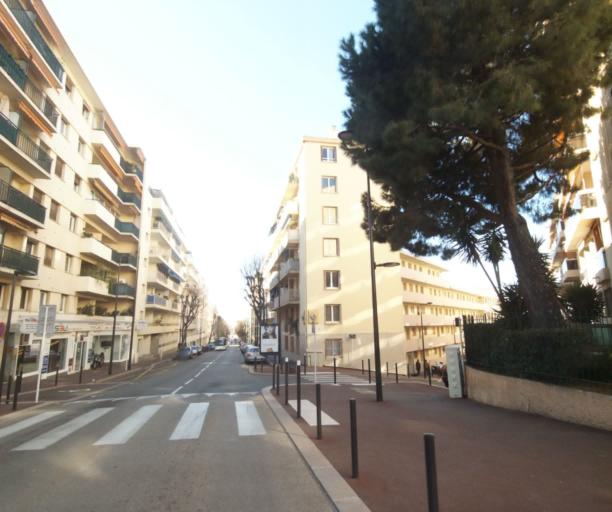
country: FR
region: Provence-Alpes-Cote d'Azur
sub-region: Departement des Alpes-Maritimes
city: Antibes
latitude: 43.5738
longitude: 7.1165
